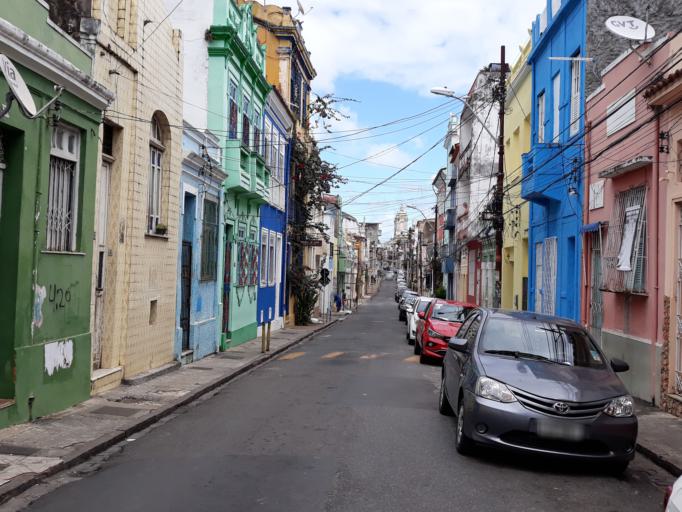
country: BR
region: Bahia
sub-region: Salvador
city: Salvador
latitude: -12.9642
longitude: -38.5044
